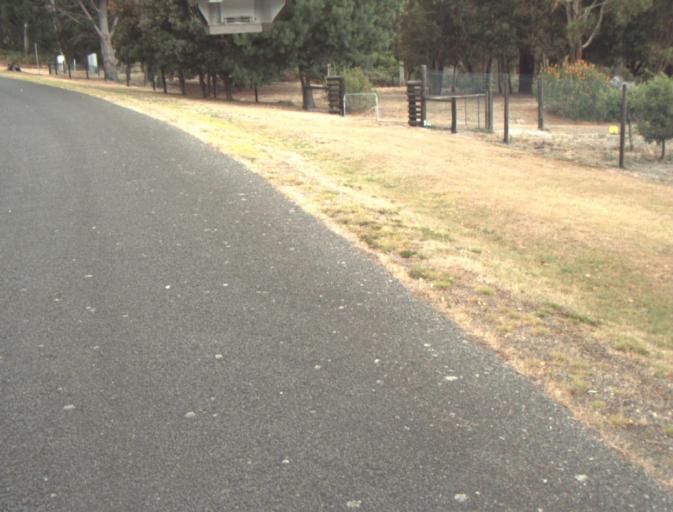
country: AU
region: Tasmania
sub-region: Launceston
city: Mayfield
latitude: -41.2818
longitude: 147.0197
